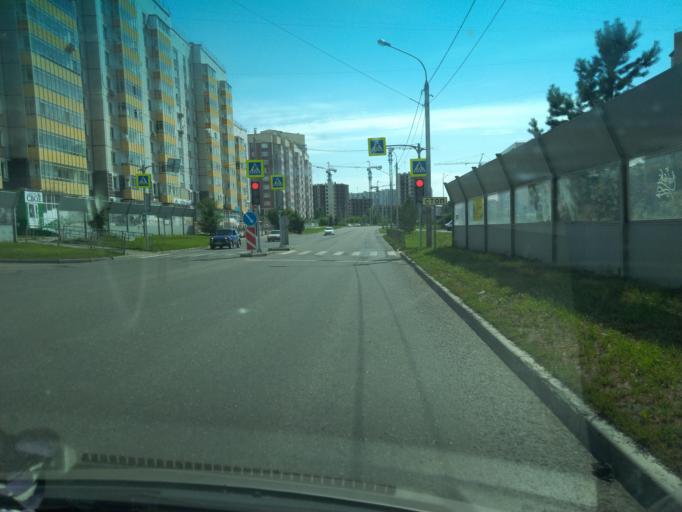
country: RU
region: Krasnoyarskiy
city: Solnechnyy
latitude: 56.0524
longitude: 92.9222
